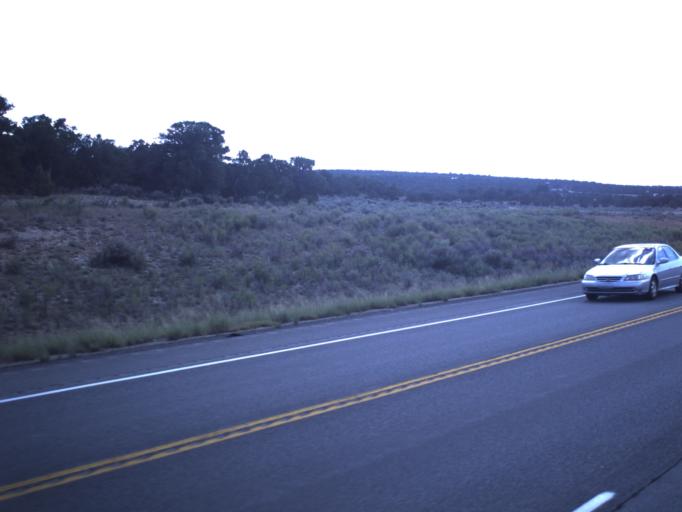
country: US
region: Utah
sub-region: Duchesne County
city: Duchesne
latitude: 40.1798
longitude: -110.6056
